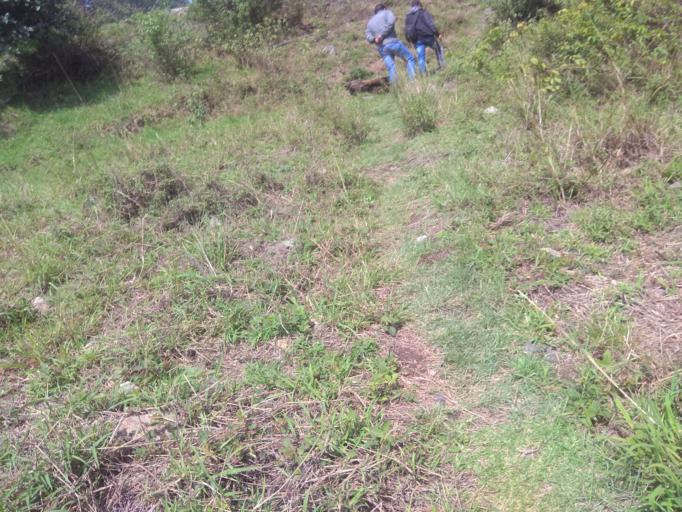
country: CO
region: Boyaca
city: Socha Viejo
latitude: 5.9831
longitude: -72.7144
